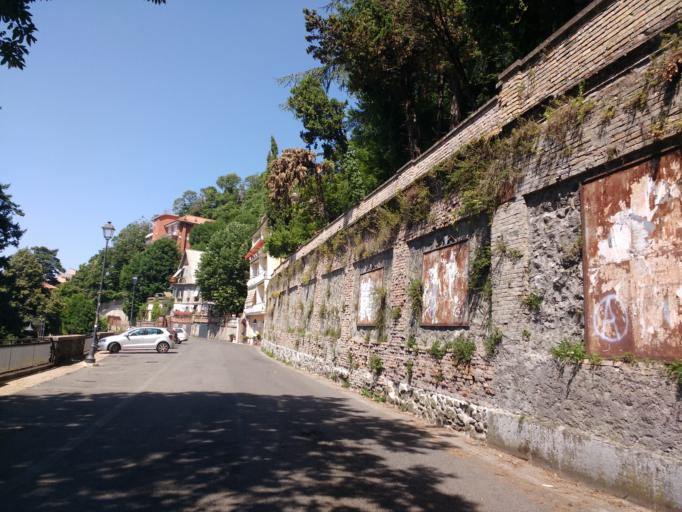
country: IT
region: Latium
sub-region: Citta metropolitana di Roma Capitale
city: Rocca di Papa
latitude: 41.7564
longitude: 12.7072
